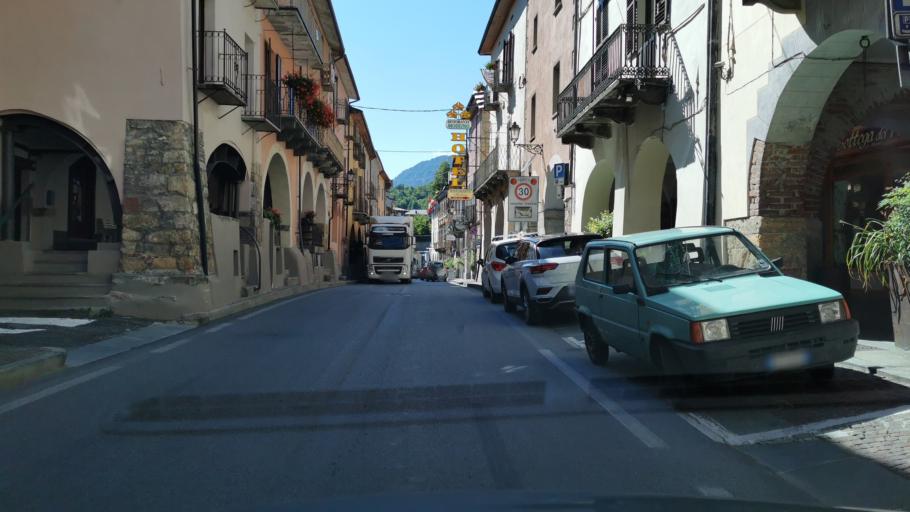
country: IT
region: Piedmont
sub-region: Provincia di Cuneo
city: Demonte
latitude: 44.3151
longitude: 7.2982
